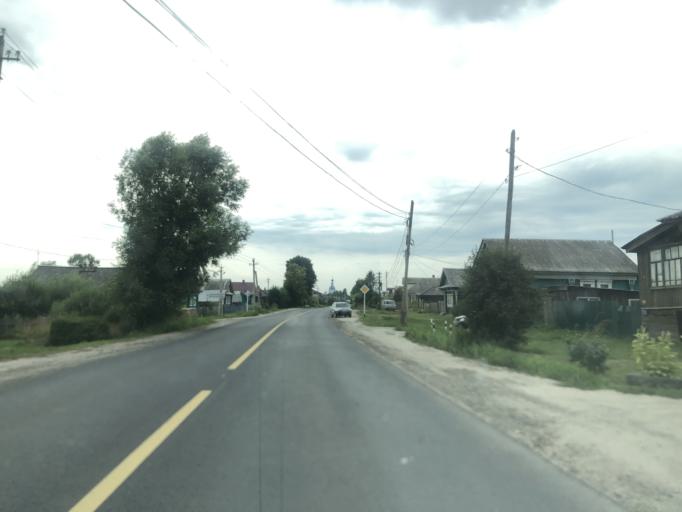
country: RU
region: Ivanovo
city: Pestyaki
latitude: 56.7054
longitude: 42.6805
